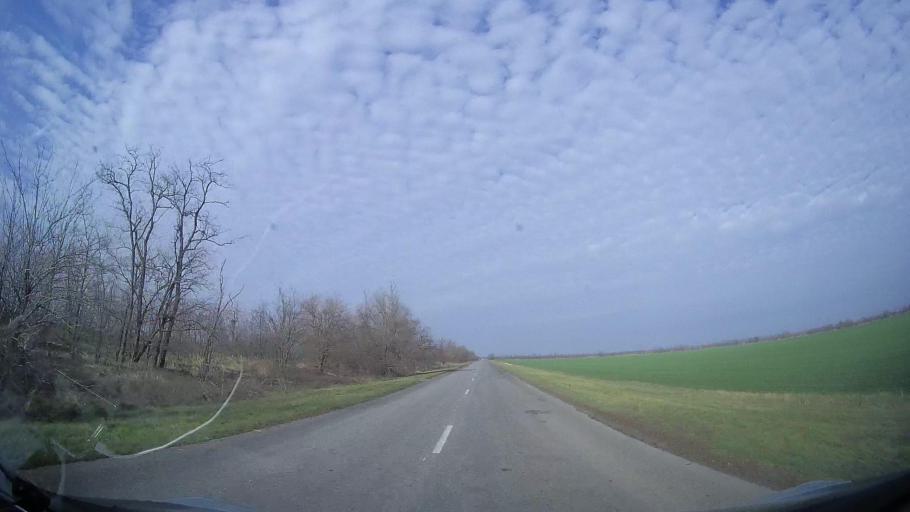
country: RU
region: Rostov
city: Gigant
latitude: 46.8697
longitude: 41.2753
